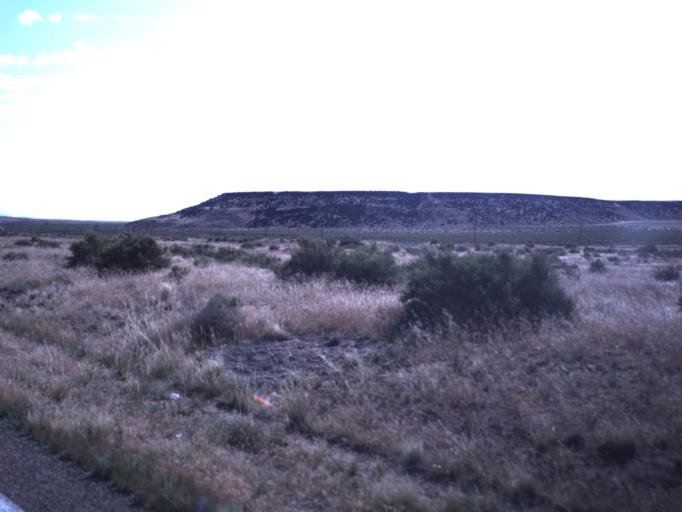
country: US
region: Utah
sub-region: Beaver County
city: Milford
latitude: 38.7514
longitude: -112.9487
